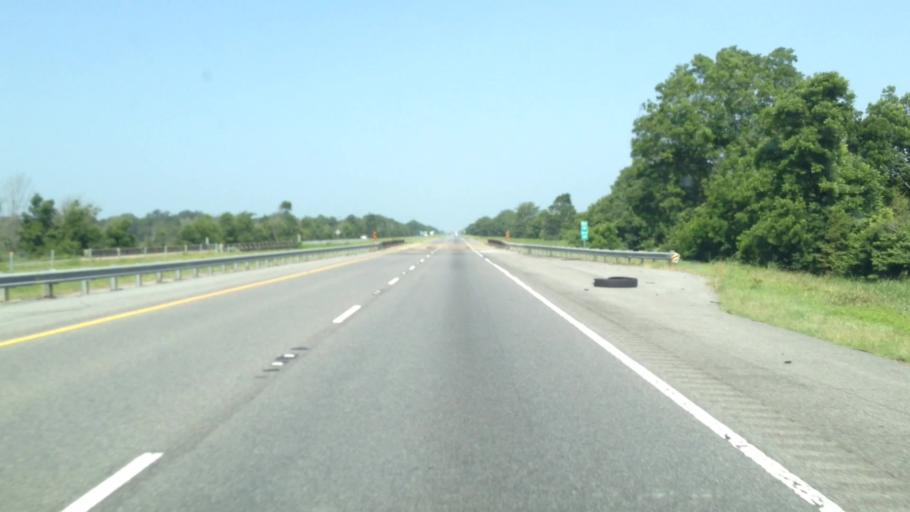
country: US
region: Louisiana
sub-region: Madison Parish
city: Tallulah
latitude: 32.4065
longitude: -91.2332
